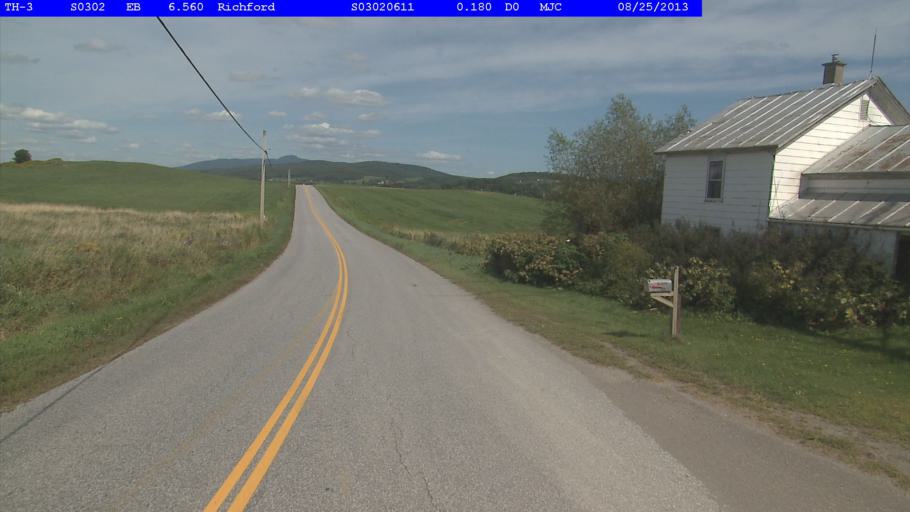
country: US
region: Vermont
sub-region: Franklin County
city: Richford
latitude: 44.9902
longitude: -72.6914
